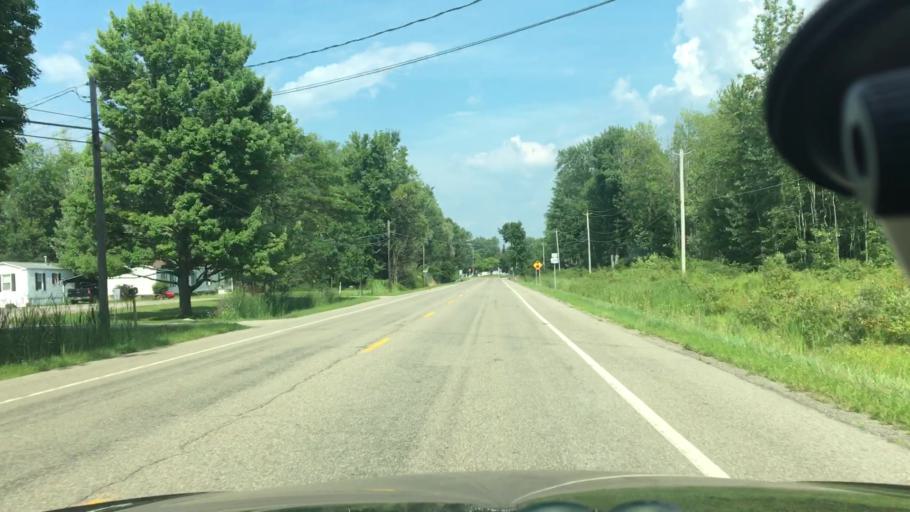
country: US
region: New York
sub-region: Chautauqua County
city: Lakewood
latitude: 42.0983
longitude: -79.3580
